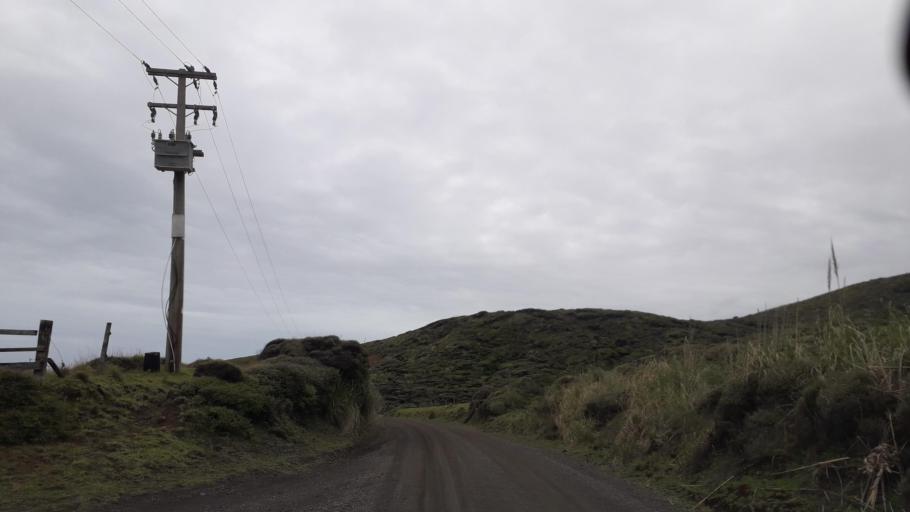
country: NZ
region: Northland
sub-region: Far North District
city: Ahipara
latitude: -35.4312
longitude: 173.2776
